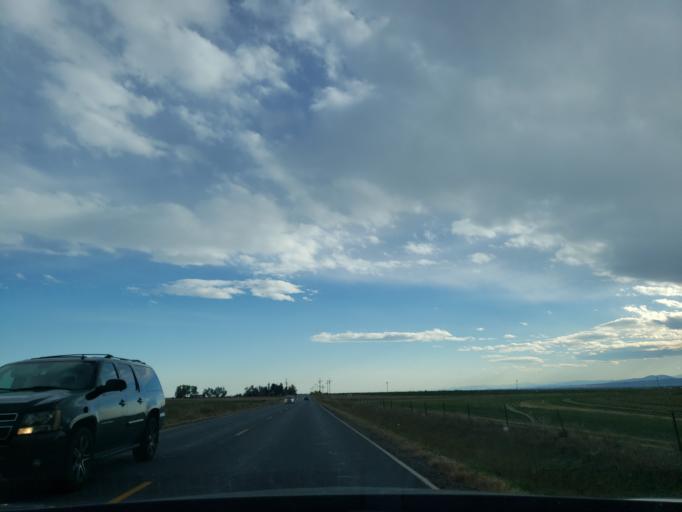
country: US
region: Colorado
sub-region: Larimer County
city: Fort Collins
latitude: 40.6274
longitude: -105.0199
